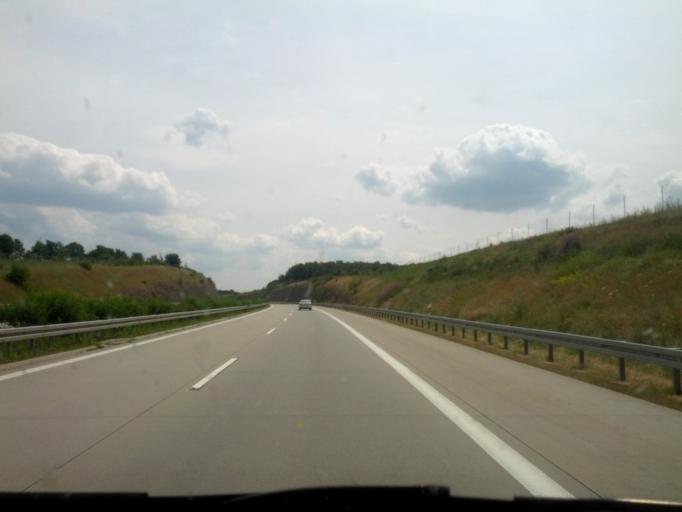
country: DE
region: Saxony
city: Liebstadt
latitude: 50.8003
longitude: 13.8815
